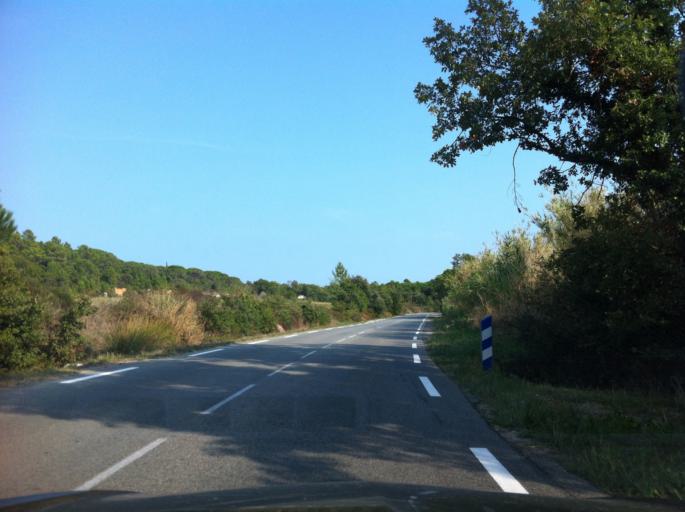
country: FR
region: Provence-Alpes-Cote d'Azur
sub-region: Departement du Var
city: Gassin
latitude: 43.2388
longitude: 6.6039
